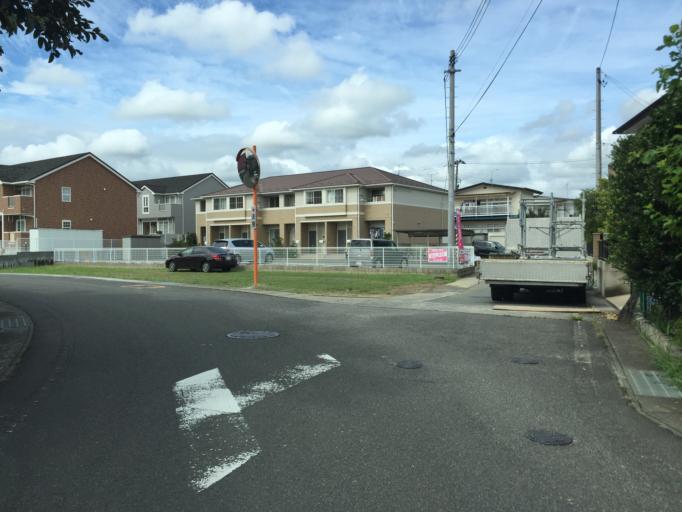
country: JP
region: Fukushima
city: Hobaramachi
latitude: 37.8062
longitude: 140.5010
